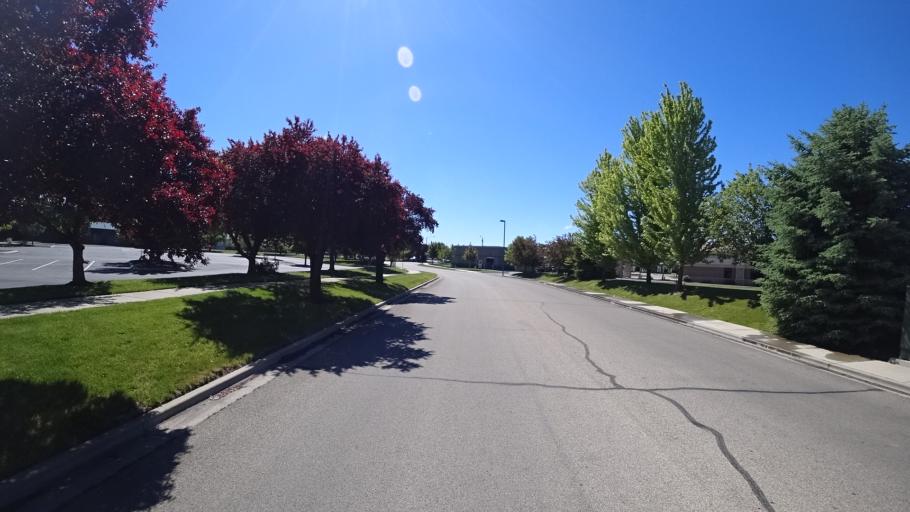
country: US
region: Idaho
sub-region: Ada County
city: Meridian
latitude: 43.6207
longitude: -116.3624
